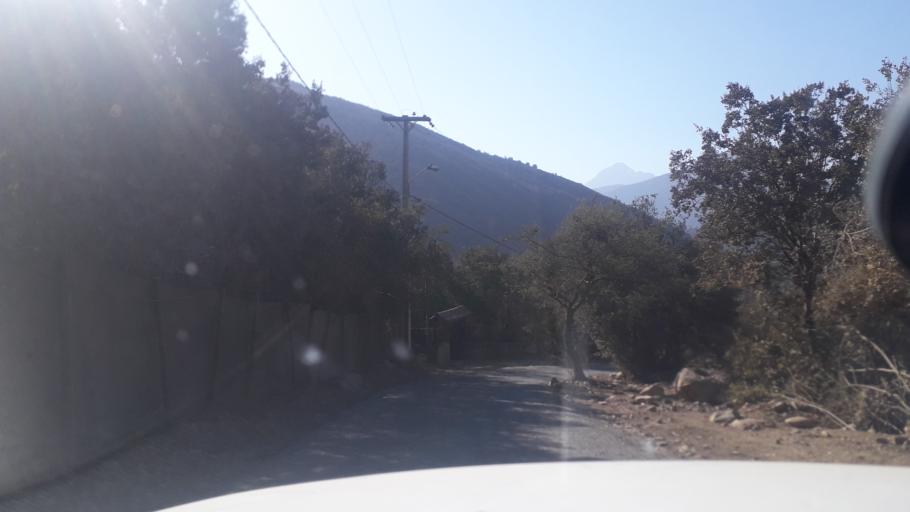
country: CL
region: Valparaiso
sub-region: Provincia de Marga Marga
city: Limache
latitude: -33.0760
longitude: -71.0991
